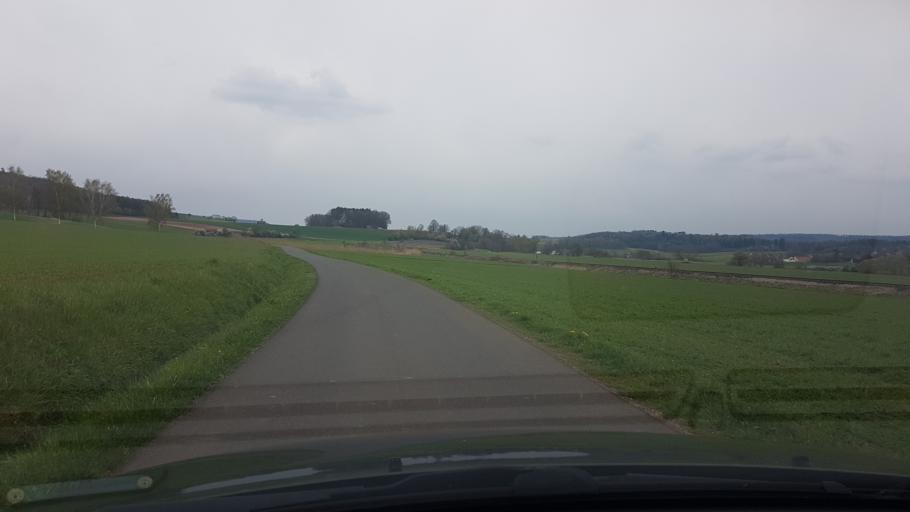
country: DE
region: Bavaria
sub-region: Regierungsbezirk Unterfranken
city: Rentweinsdorf
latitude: 50.0586
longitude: 10.8166
